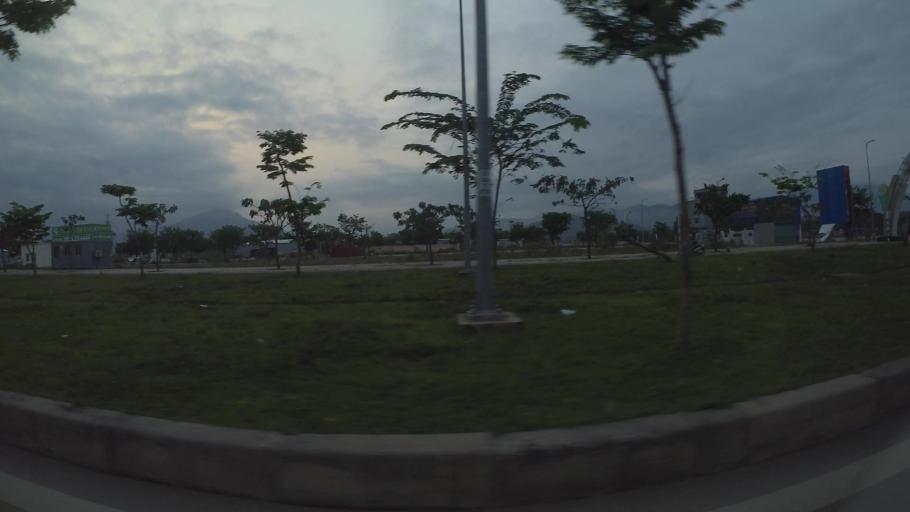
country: VN
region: Da Nang
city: Lien Chieu
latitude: 16.0959
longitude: 108.1124
